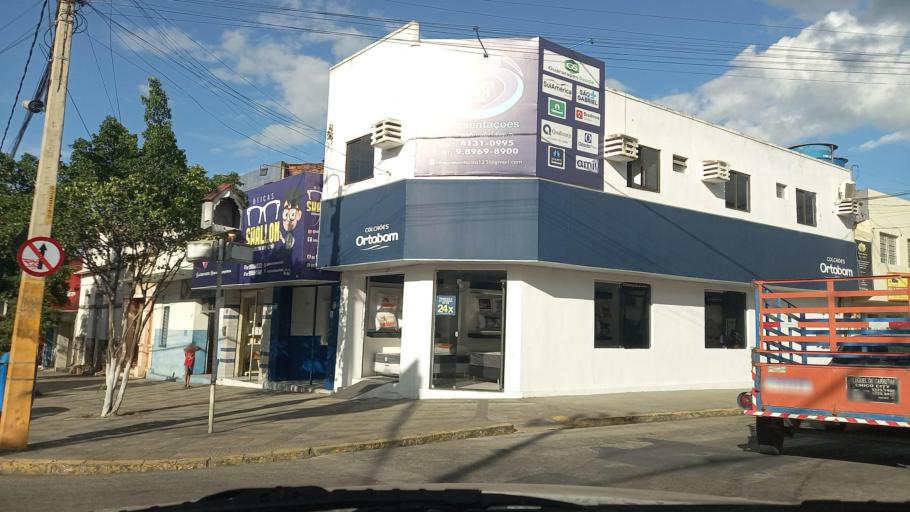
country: BR
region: Pernambuco
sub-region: Gravata
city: Gravata
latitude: -8.2044
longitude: -35.5694
